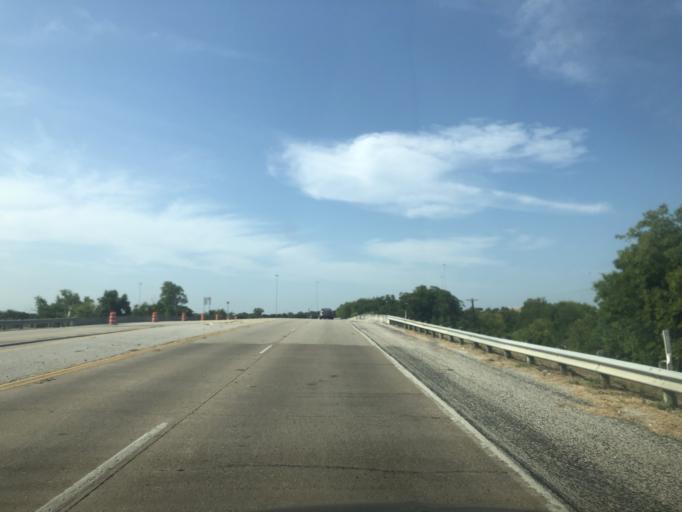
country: US
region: Texas
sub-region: Tarrant County
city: Benbrook
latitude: 32.6900
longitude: -97.4576
